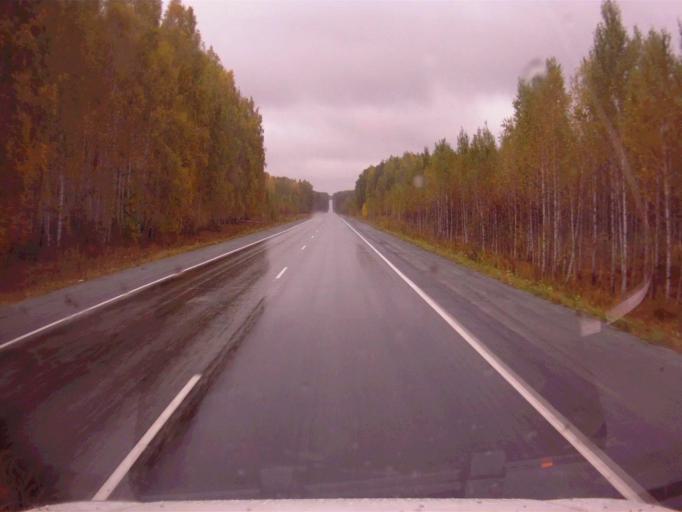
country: RU
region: Chelyabinsk
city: Tayginka
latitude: 55.5104
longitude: 60.6383
